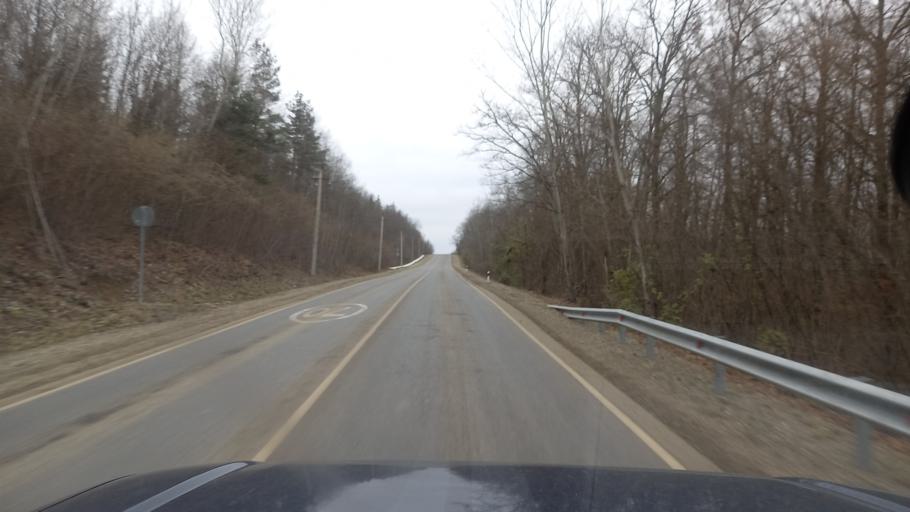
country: RU
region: Krasnodarskiy
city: Saratovskaya
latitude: 44.5415
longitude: 39.2983
